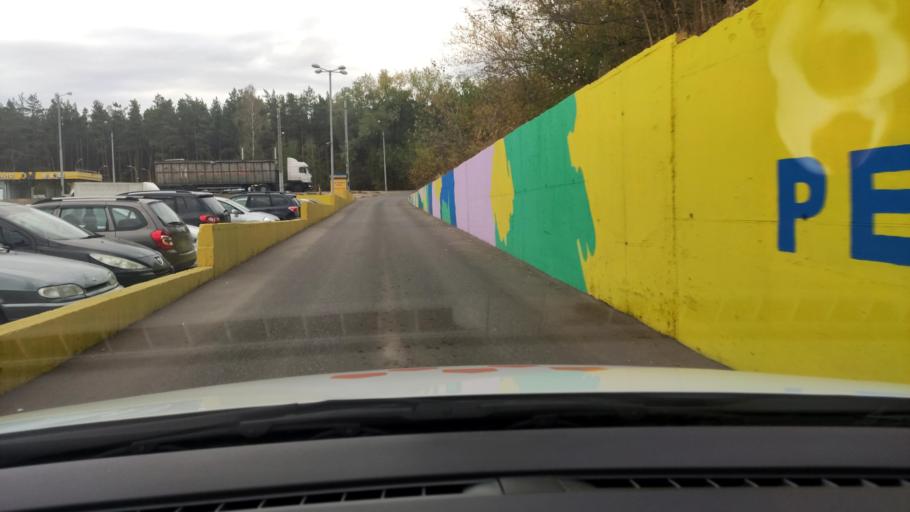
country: RU
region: Voronezj
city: Pridonskoy
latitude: 51.6463
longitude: 39.1146
